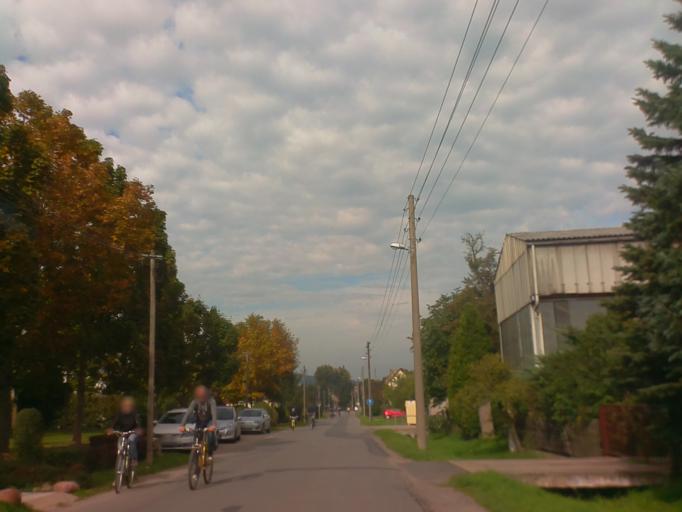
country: DE
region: Thuringia
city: Rothenstein
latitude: 50.8437
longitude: 11.6092
